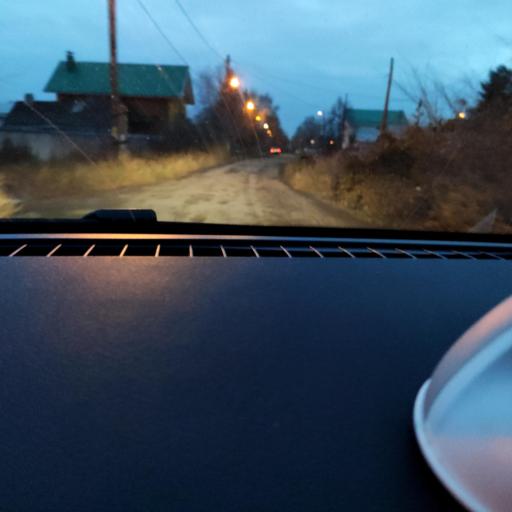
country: RU
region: Samara
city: Smyshlyayevka
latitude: 53.2529
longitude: 50.3533
